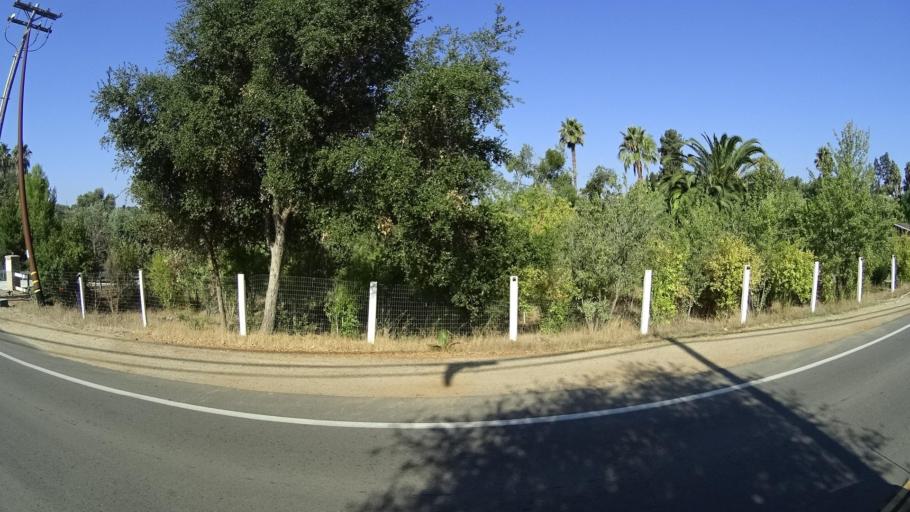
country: US
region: California
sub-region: San Diego County
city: Fallbrook
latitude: 33.3311
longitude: -117.2449
